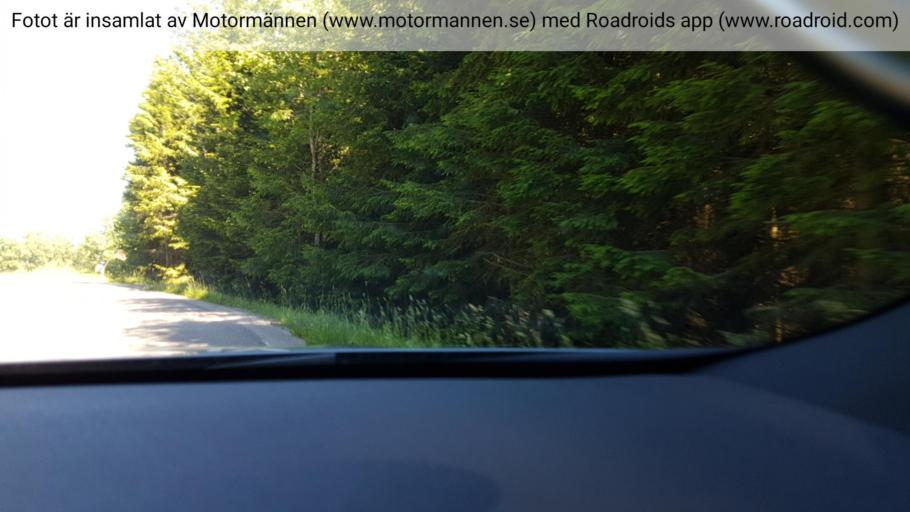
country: SE
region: Vaestra Goetaland
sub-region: Falkopings Kommun
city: Floby
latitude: 58.0683
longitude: 13.4438
